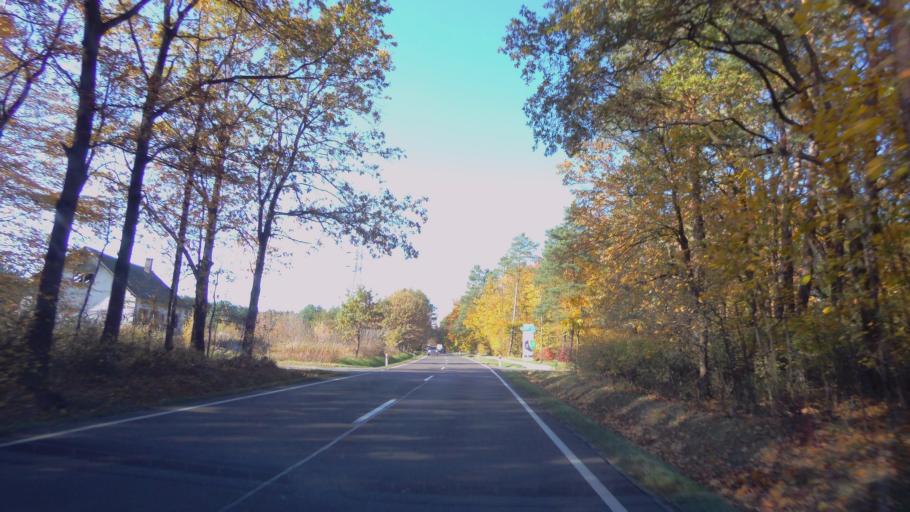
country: PL
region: Subcarpathian Voivodeship
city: Nowa Sarzyna
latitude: 50.2951
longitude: 22.3740
